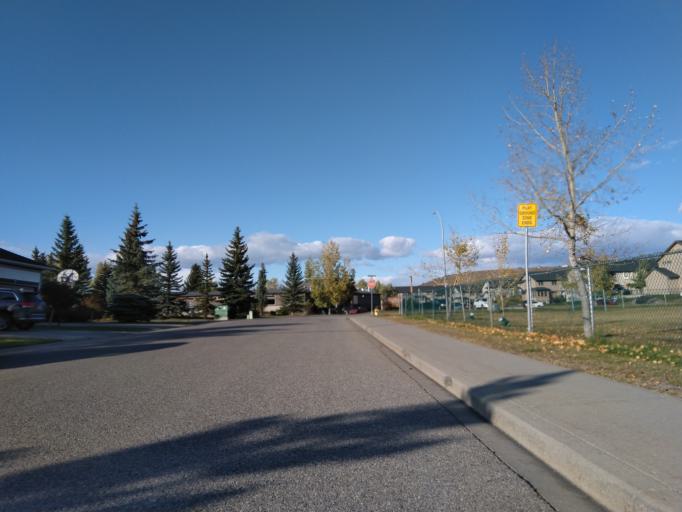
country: CA
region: Alberta
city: Cochrane
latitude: 51.1764
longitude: -114.4691
